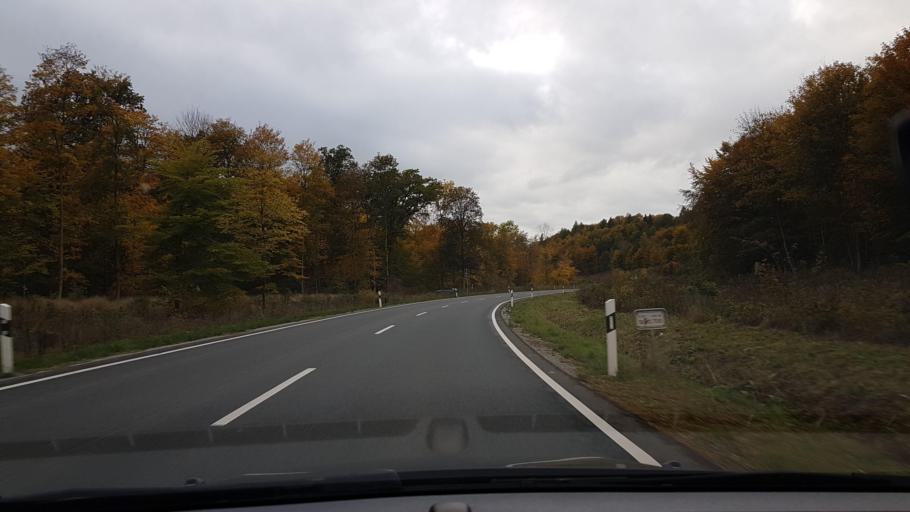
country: DE
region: Lower Saxony
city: Bad Grund
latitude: 51.8287
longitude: 10.2071
